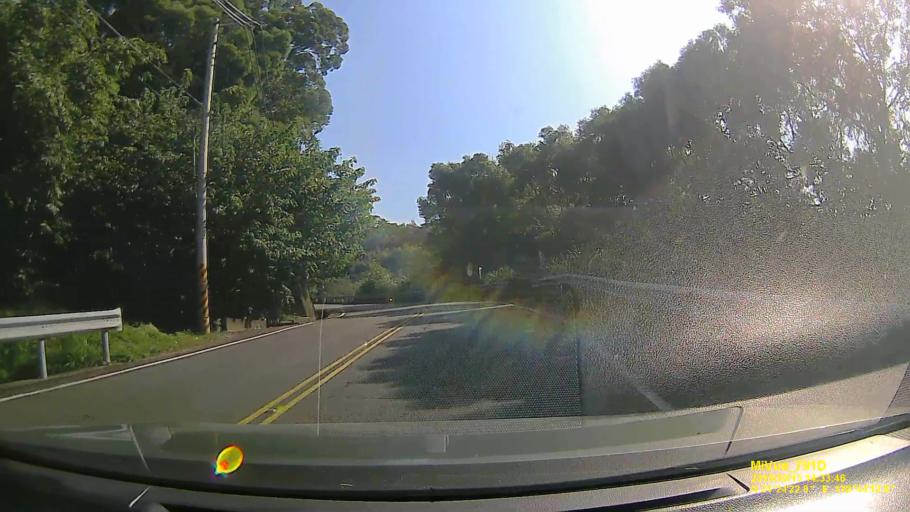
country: TW
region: Taiwan
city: Fengyuan
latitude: 24.4063
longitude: 120.7369
